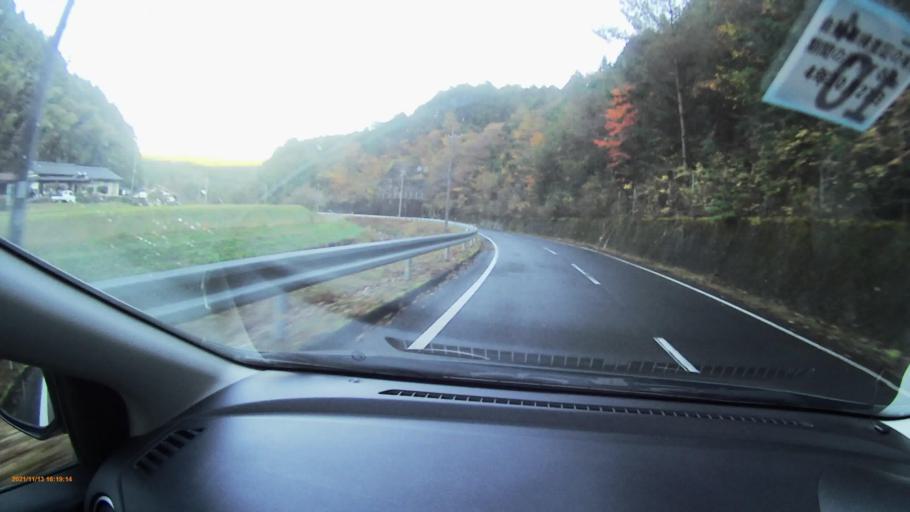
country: JP
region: Gifu
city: Nakatsugawa
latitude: 35.5693
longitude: 137.5065
